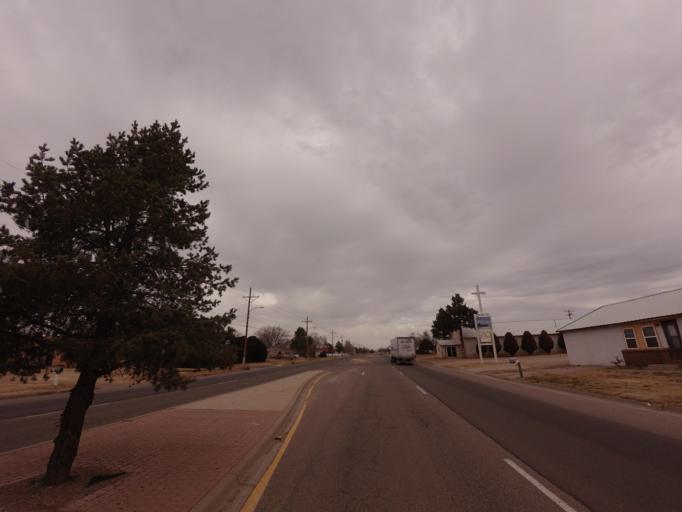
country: US
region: New Mexico
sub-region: Curry County
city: Clovis
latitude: 34.3797
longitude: -103.1964
